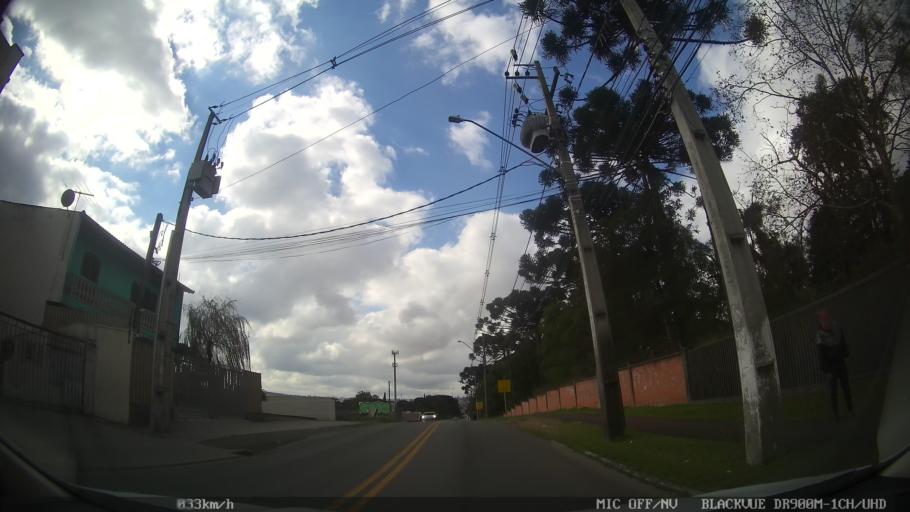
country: BR
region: Parana
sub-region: Pinhais
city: Pinhais
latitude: -25.3745
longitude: -49.2162
